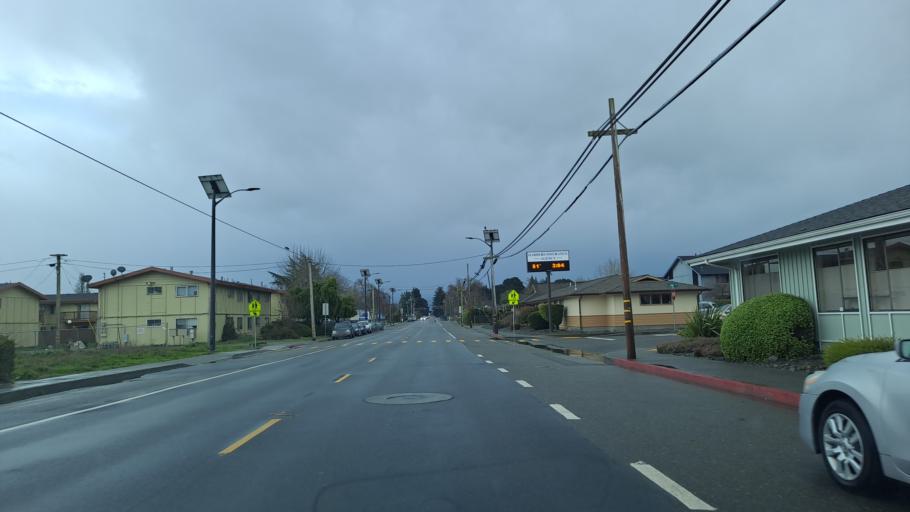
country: US
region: California
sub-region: Humboldt County
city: Fortuna
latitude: 40.5931
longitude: -124.1545
